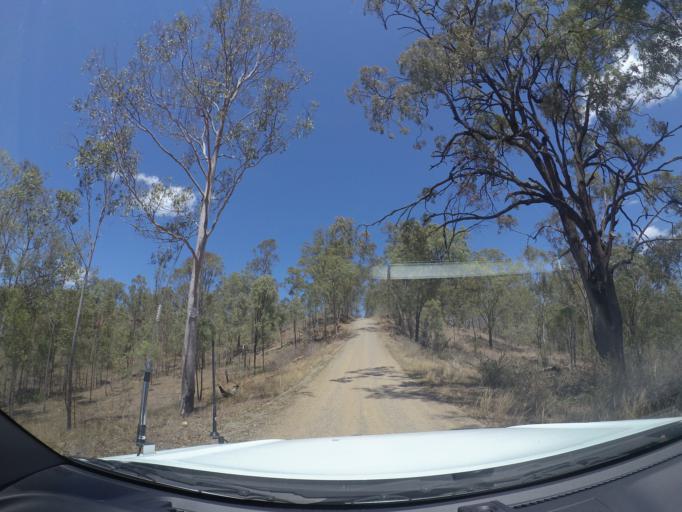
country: AU
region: Queensland
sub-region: Ipswich
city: Deebing Heights
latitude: -27.8270
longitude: 152.8361
